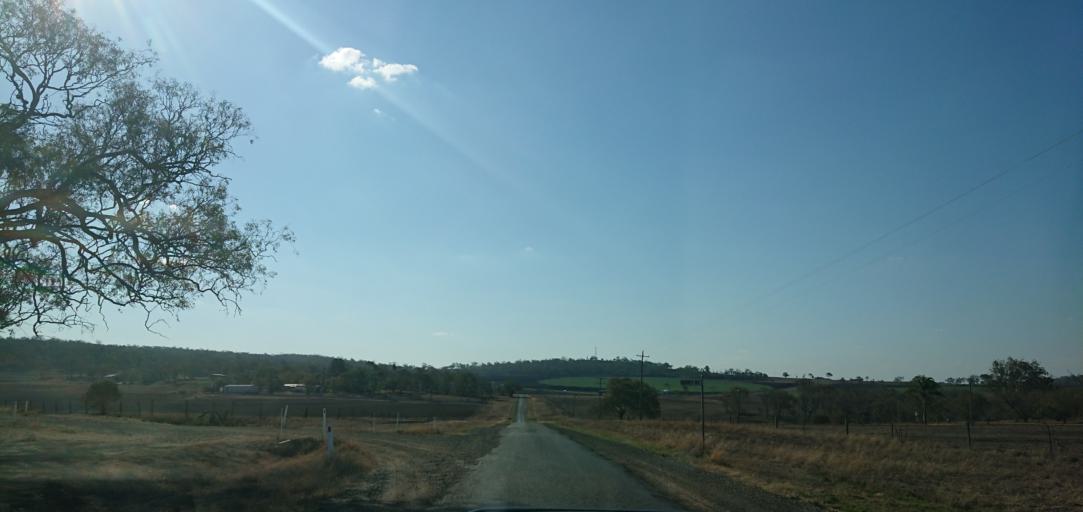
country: AU
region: Queensland
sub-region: Toowoomba
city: Westbrook
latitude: -27.7160
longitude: 151.7198
